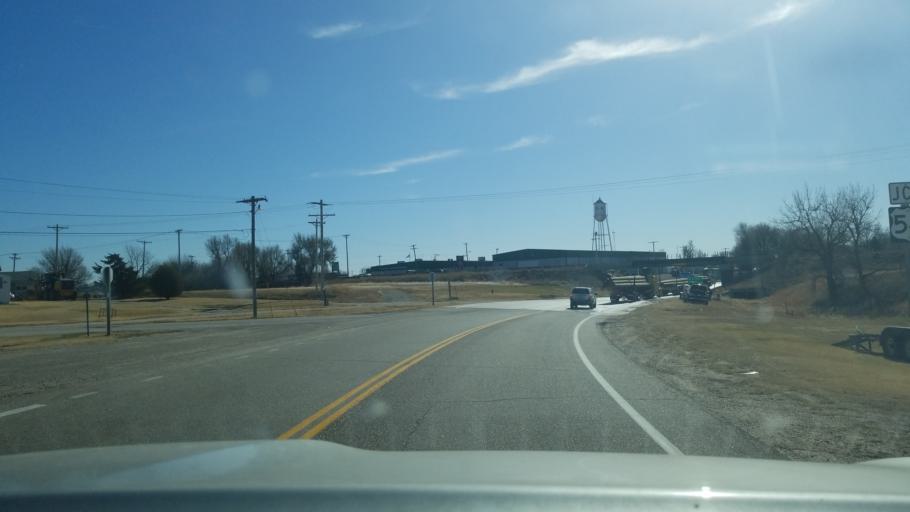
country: US
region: Kansas
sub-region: Kiowa County
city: Greensburg
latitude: 37.5531
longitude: -99.6371
